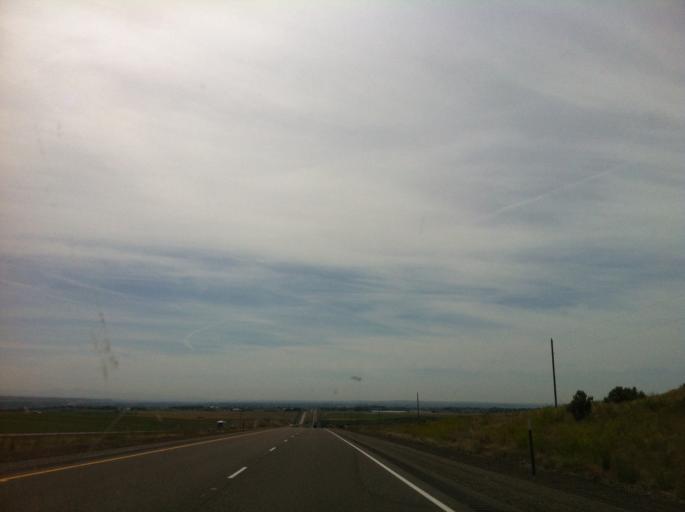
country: US
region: Oregon
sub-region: Malheur County
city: Ontario
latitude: 44.1105
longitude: -117.0548
